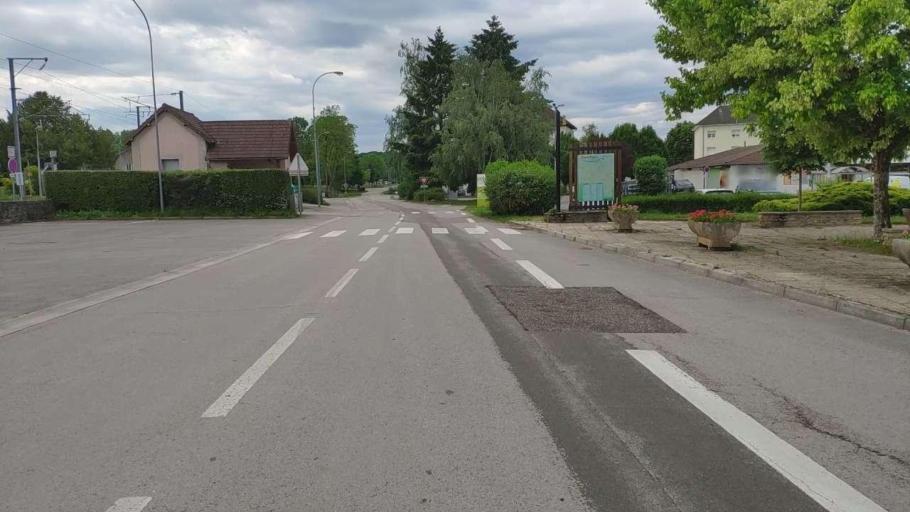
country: FR
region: Franche-Comte
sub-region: Departement du Jura
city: Perrigny
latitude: 46.7633
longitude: 5.5975
